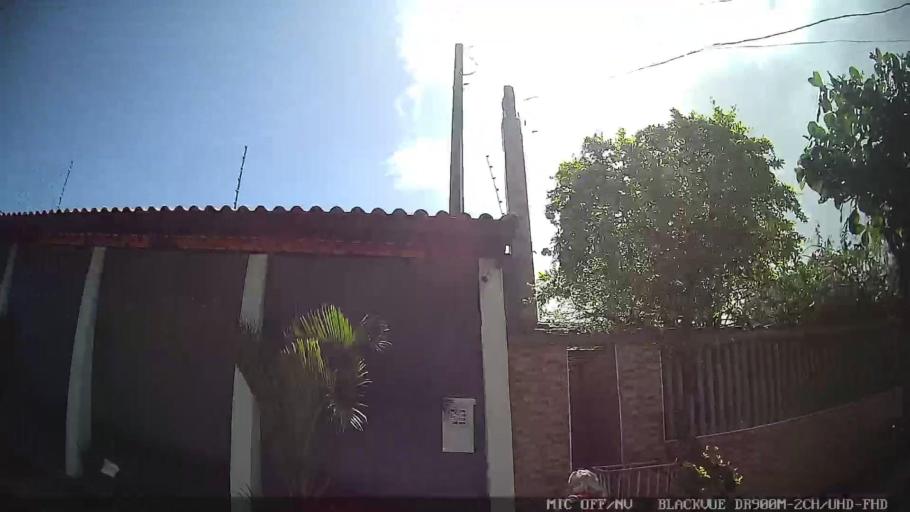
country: BR
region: Sao Paulo
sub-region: Itanhaem
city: Itanhaem
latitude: -24.1683
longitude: -46.7566
